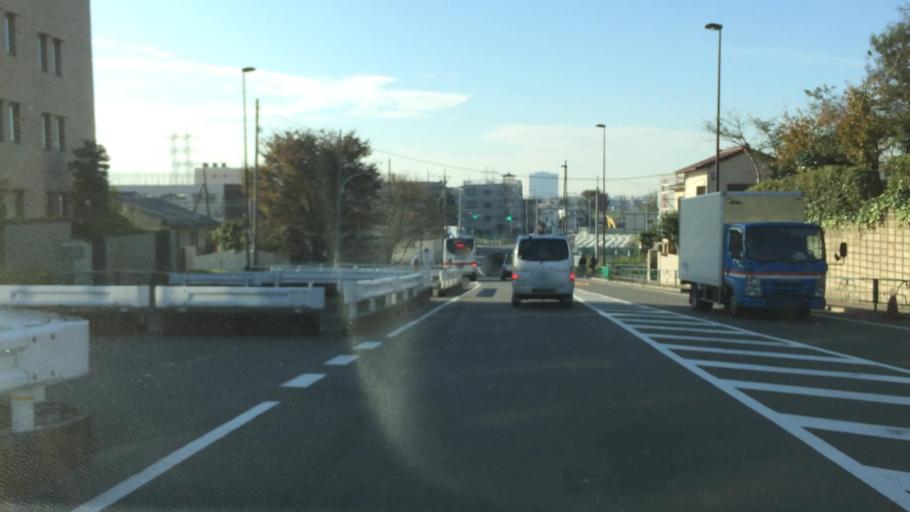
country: JP
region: Tokyo
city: Tokyo
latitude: 35.6012
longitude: 139.6472
